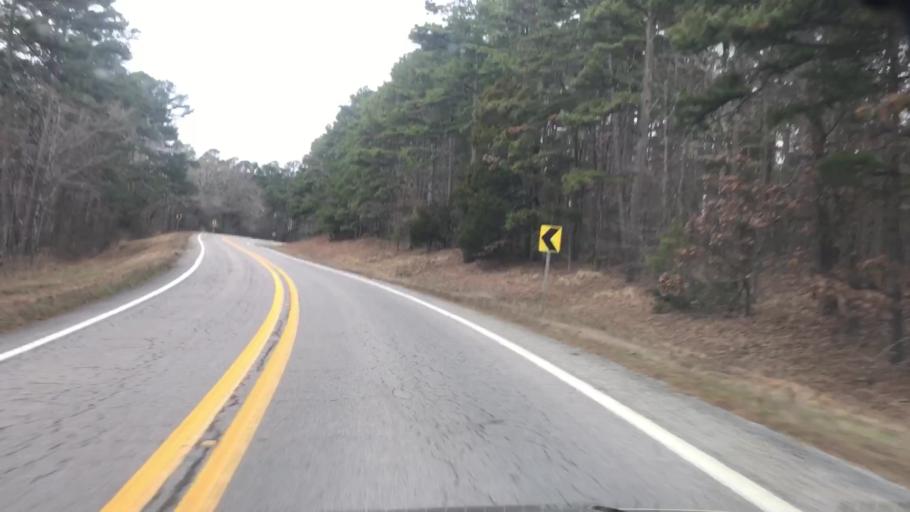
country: US
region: Arkansas
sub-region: Montgomery County
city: Mount Ida
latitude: 34.6706
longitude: -93.7784
